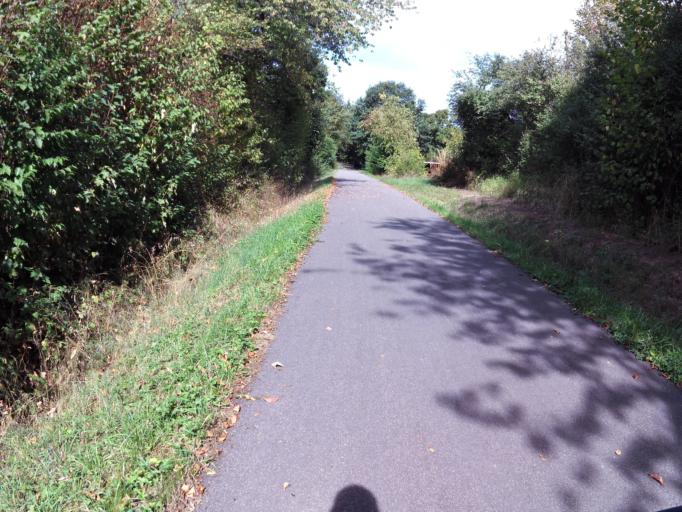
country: DE
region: Rheinland-Pfalz
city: Kickeshausen
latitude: 50.0712
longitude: 6.2567
